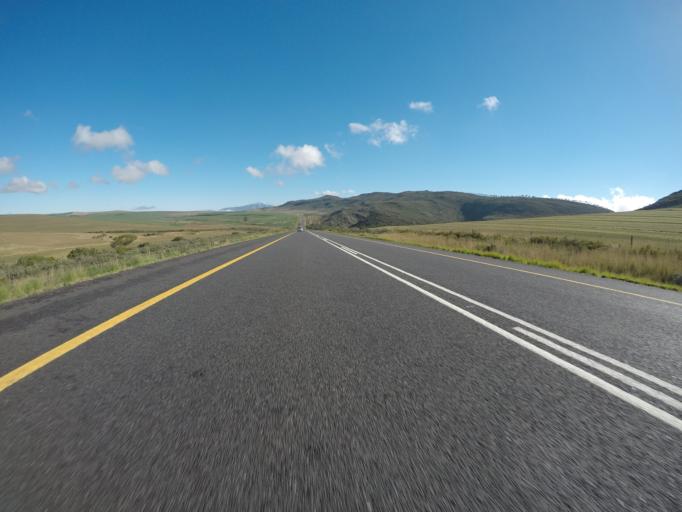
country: ZA
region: Western Cape
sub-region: Overberg District Municipality
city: Swellendam
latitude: -34.1046
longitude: 20.2333
